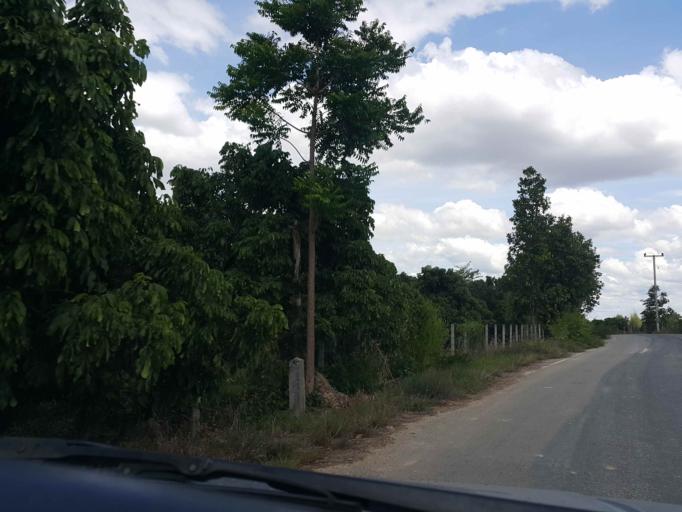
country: TH
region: Chiang Mai
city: Doi Lo
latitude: 18.4759
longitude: 98.7497
